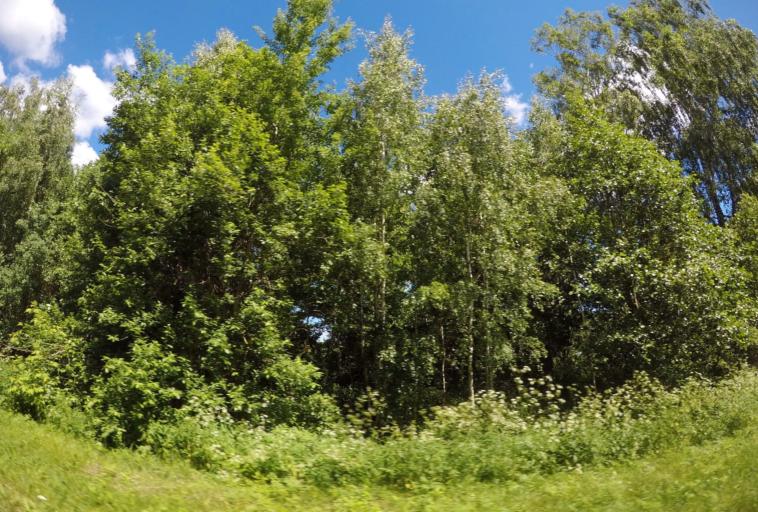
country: BY
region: Grodnenskaya
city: Hal'shany
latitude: 54.1808
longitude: 26.1005
